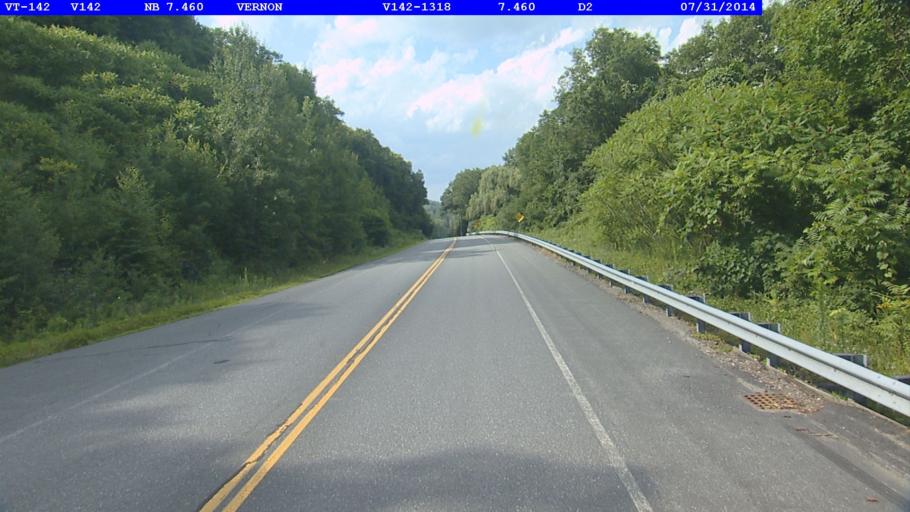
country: US
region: Vermont
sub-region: Windham County
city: Brattleboro
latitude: 42.8079
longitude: -72.5431
